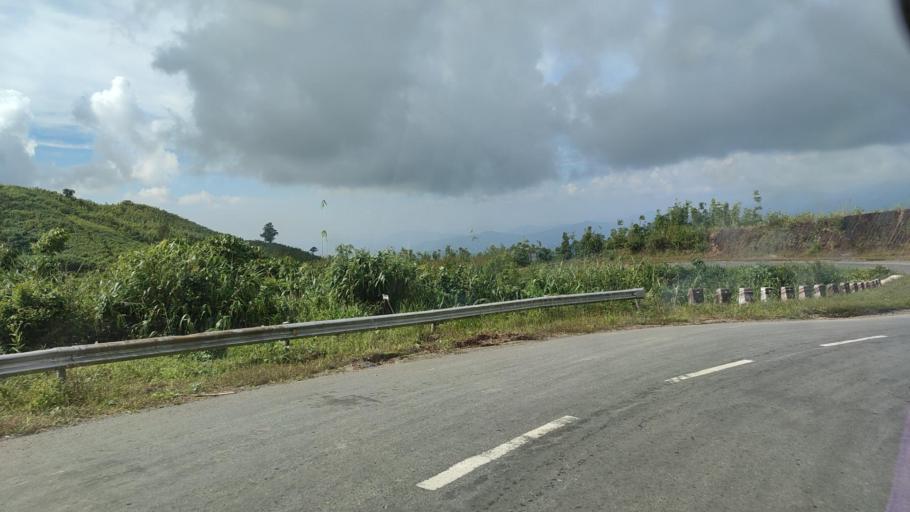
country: MM
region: Magway
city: Minbu
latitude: 19.8335
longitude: 94.2881
